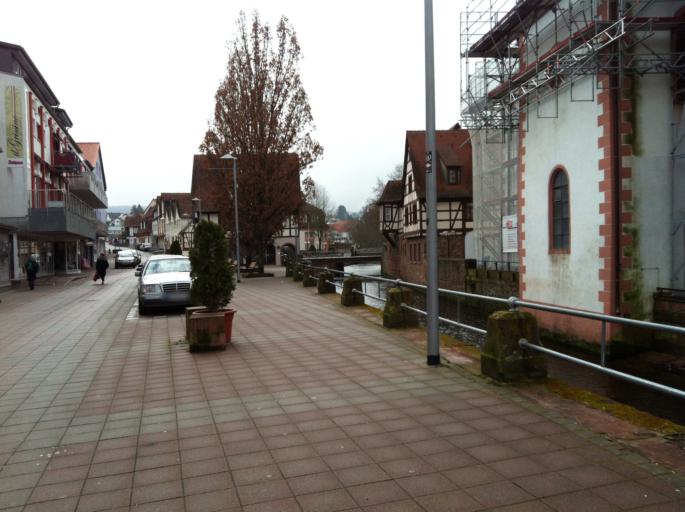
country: DE
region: Hesse
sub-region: Regierungsbezirk Darmstadt
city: Erbach
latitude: 49.6582
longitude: 8.9929
